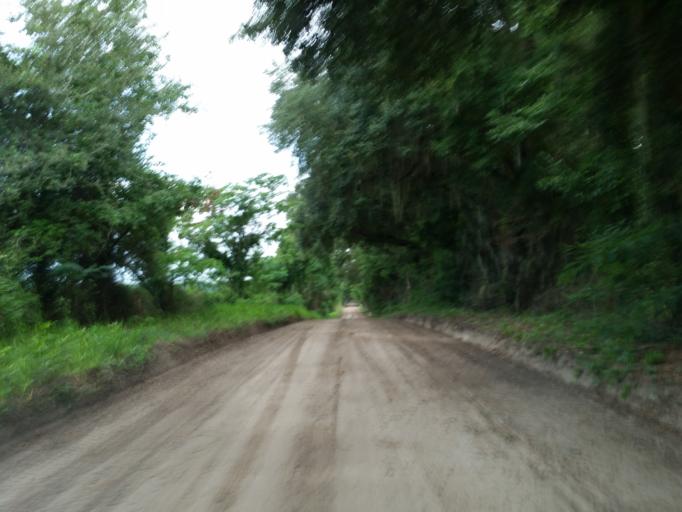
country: US
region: Florida
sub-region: Alachua County
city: High Springs
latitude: 29.9640
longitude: -82.5595
